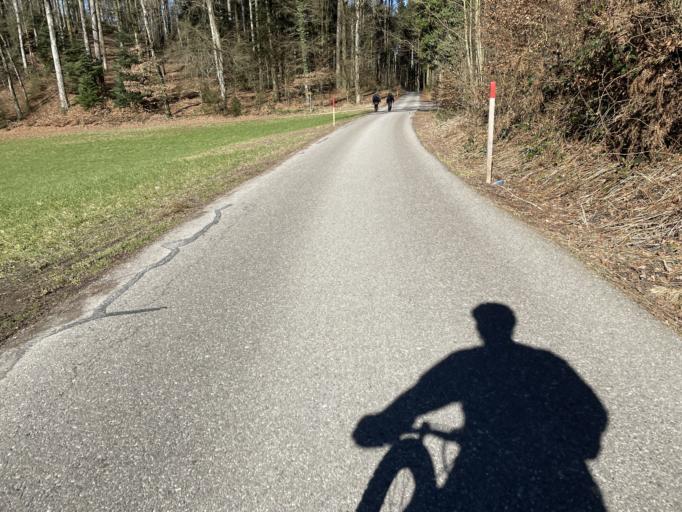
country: CH
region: Bern
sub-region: Bern-Mittelland District
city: Bariswil
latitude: 47.0069
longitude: 7.5357
